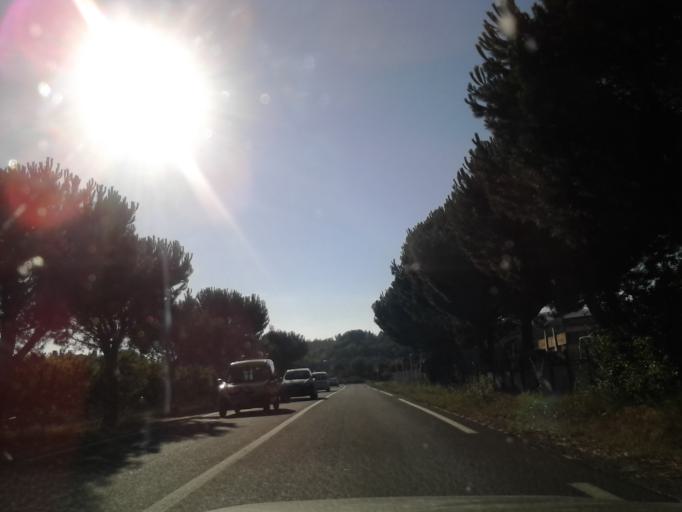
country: FR
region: Languedoc-Roussillon
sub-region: Departement des Pyrenees-Orientales
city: Prades
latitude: 42.6230
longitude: 2.4369
